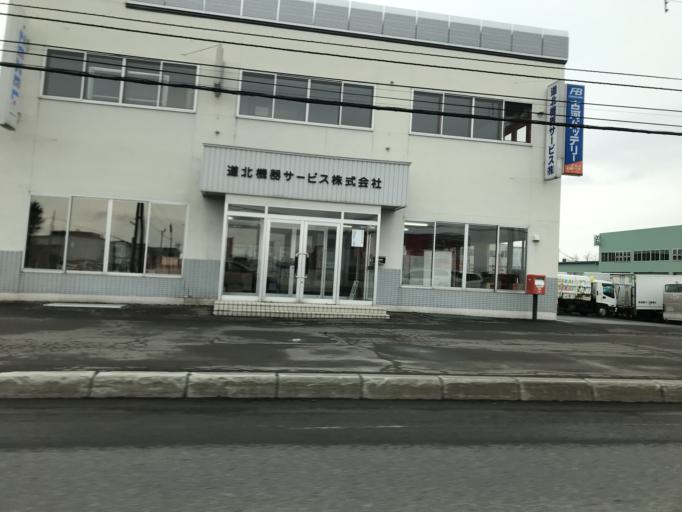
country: JP
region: Hokkaido
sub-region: Asahikawa-shi
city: Asahikawa
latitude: 43.8174
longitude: 142.4057
